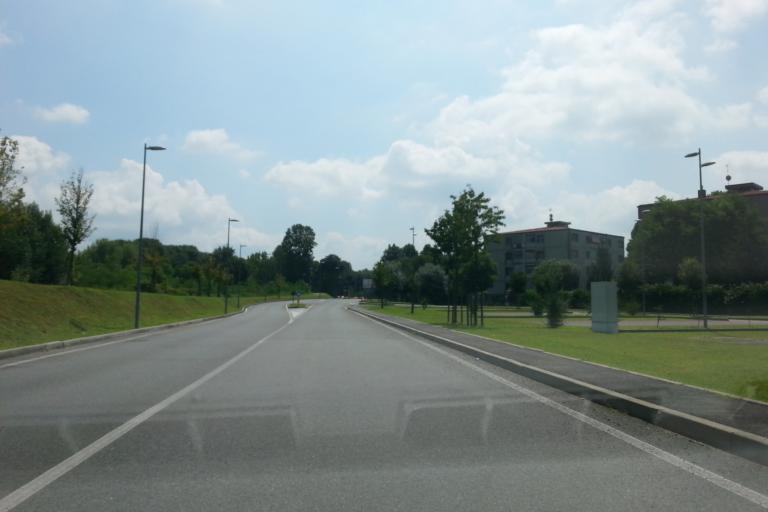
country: IT
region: Piedmont
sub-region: Provincia di Torino
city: Venaria Reale
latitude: 45.1387
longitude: 7.6250
